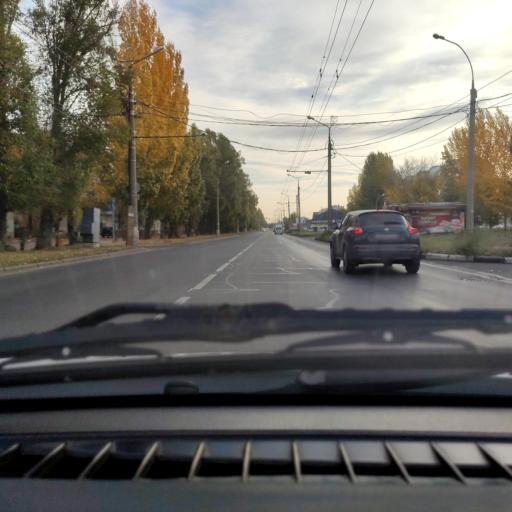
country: RU
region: Samara
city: Tol'yatti
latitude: 53.5107
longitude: 49.4373
